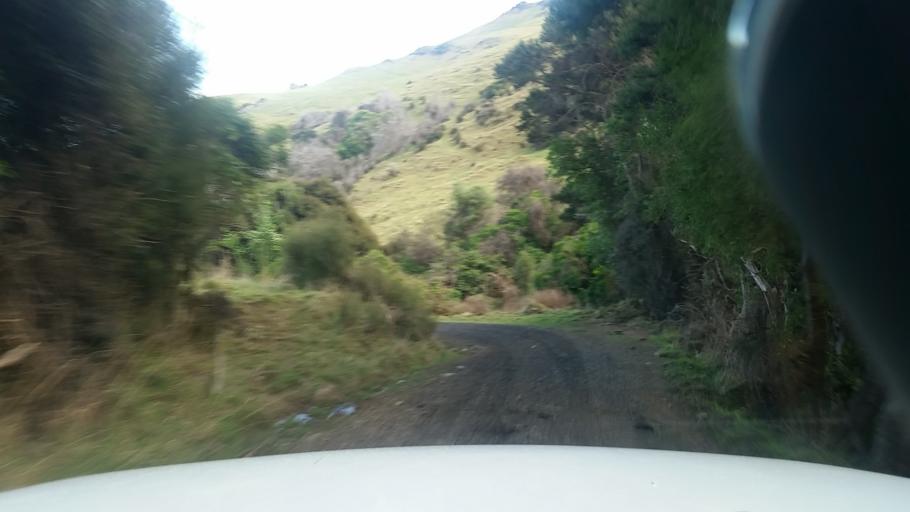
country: NZ
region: Canterbury
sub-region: Christchurch City
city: Christchurch
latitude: -43.7568
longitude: 172.9977
